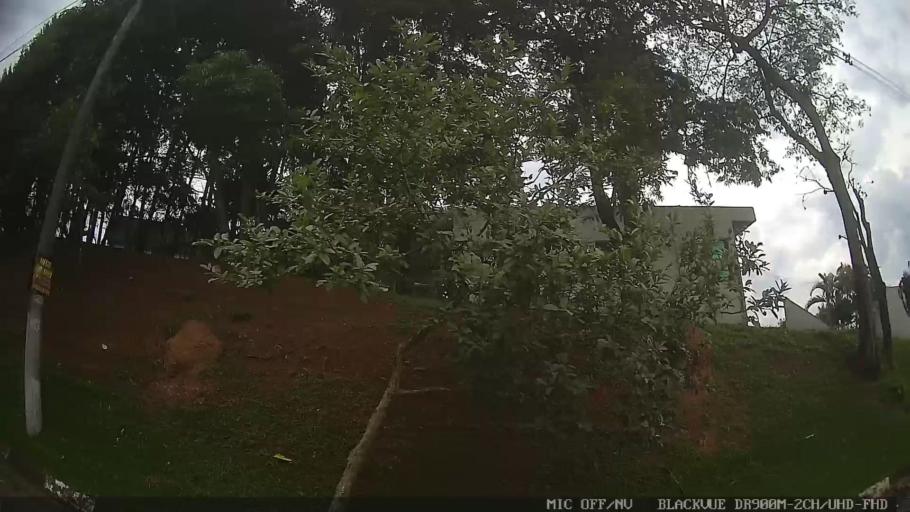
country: BR
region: Sao Paulo
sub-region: Aruja
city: Aruja
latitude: -23.4467
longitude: -46.3092
